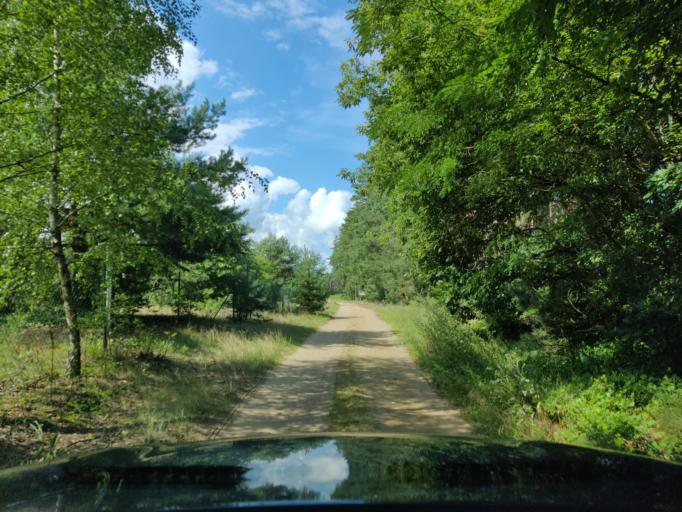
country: PL
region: Masovian Voivodeship
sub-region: Powiat pultuski
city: Obryte
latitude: 52.7451
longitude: 21.1855
